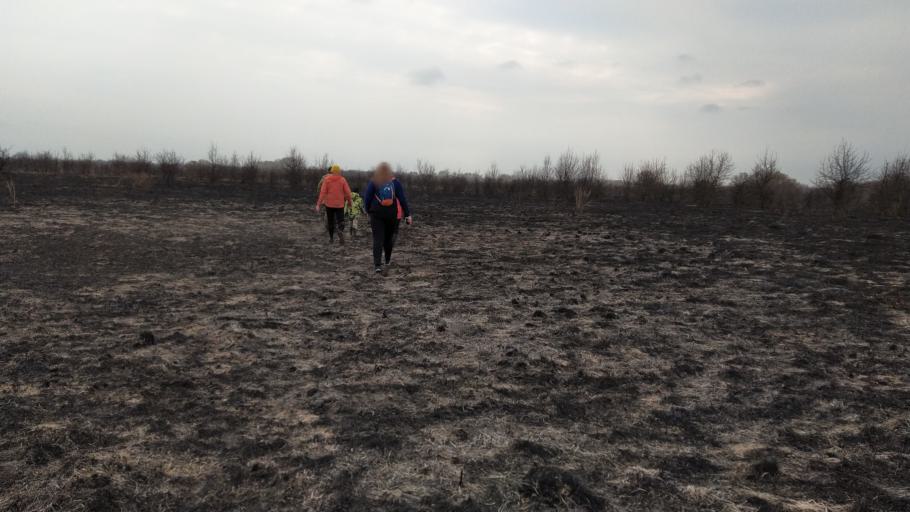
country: RU
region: Rostov
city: Semikarakorsk
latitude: 47.5487
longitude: 40.6808
